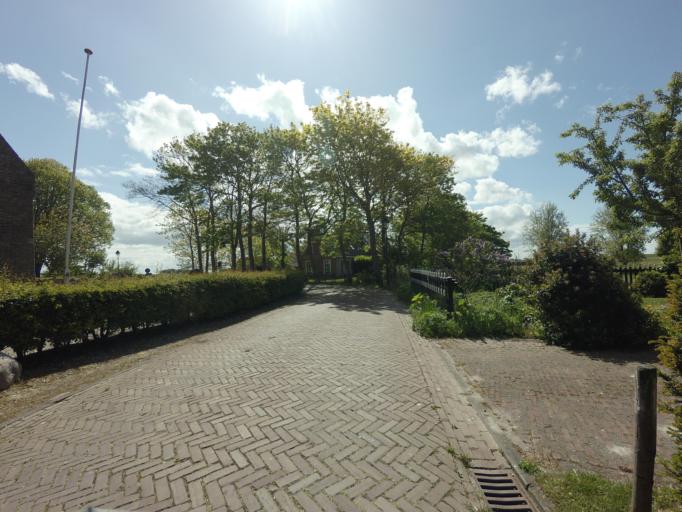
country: NL
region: Friesland
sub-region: Sudwest Fryslan
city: Makkum
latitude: 53.0383
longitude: 5.4077
